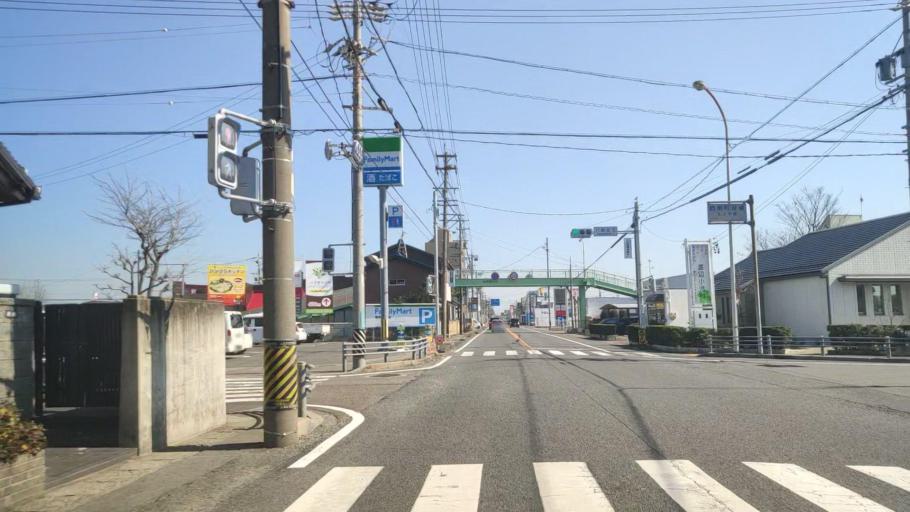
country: JP
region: Gifu
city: Kasamatsucho
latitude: 35.3939
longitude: 136.7818
